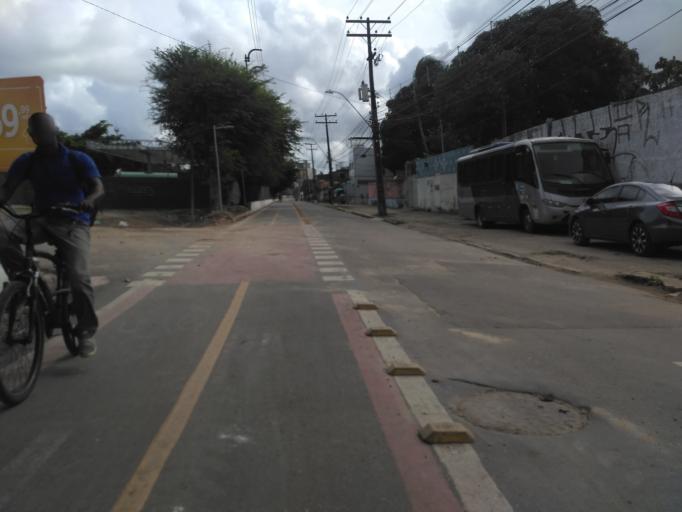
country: BR
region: Pernambuco
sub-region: Recife
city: Recife
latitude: -8.0381
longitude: -34.8766
